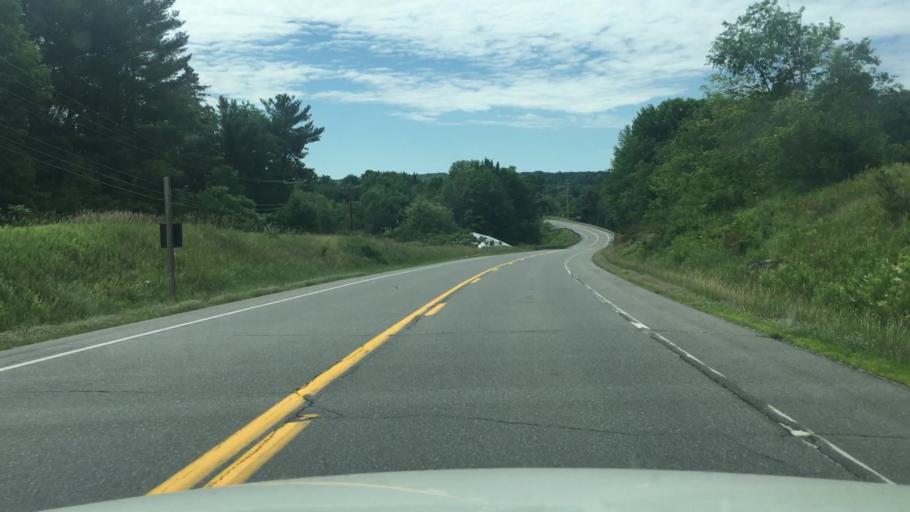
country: US
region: Maine
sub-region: Waldo County
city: Troy
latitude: 44.5843
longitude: -69.2795
